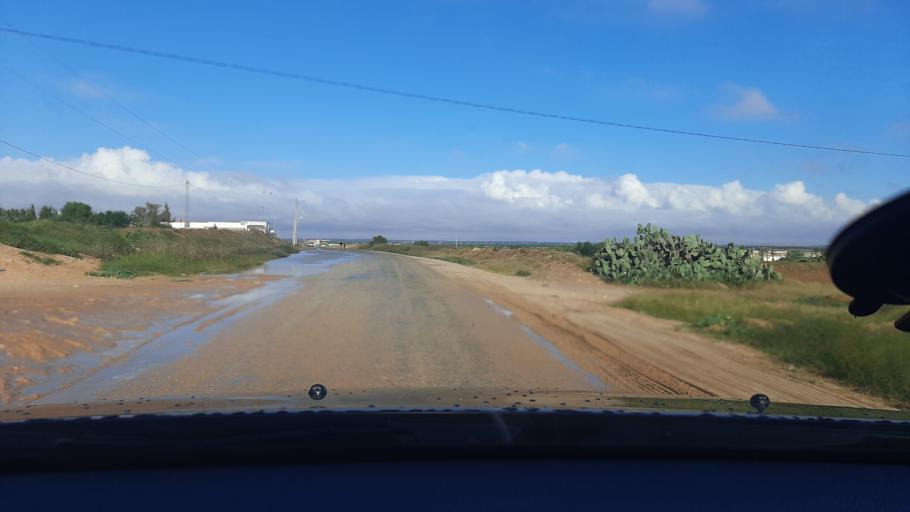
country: TN
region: Safaqis
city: Sfax
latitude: 34.8809
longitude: 10.6324
